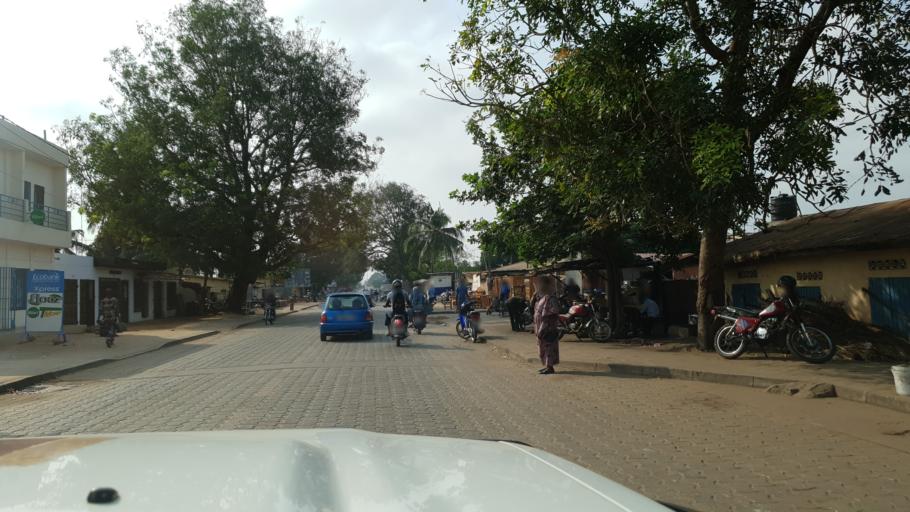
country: TG
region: Maritime
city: Lome
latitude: 6.1620
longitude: 1.2150
